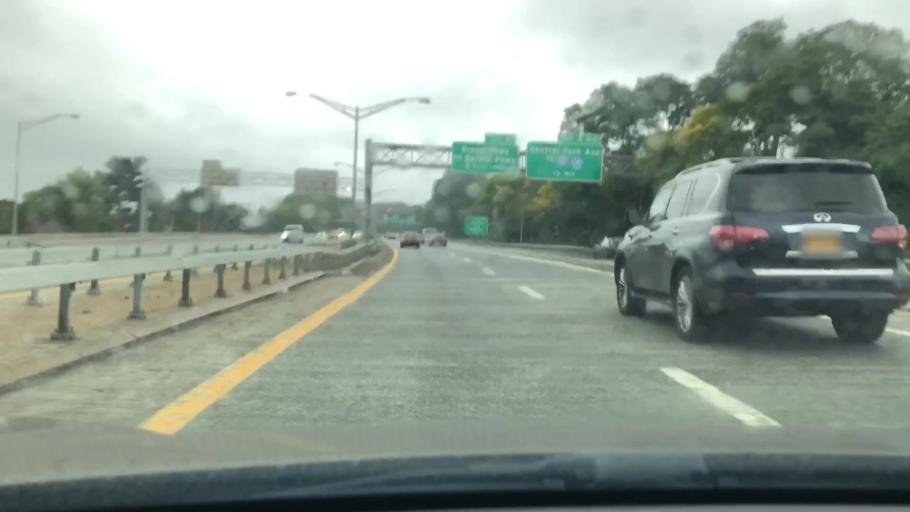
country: US
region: New York
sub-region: Westchester County
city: Yonkers
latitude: 40.9325
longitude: -73.8709
